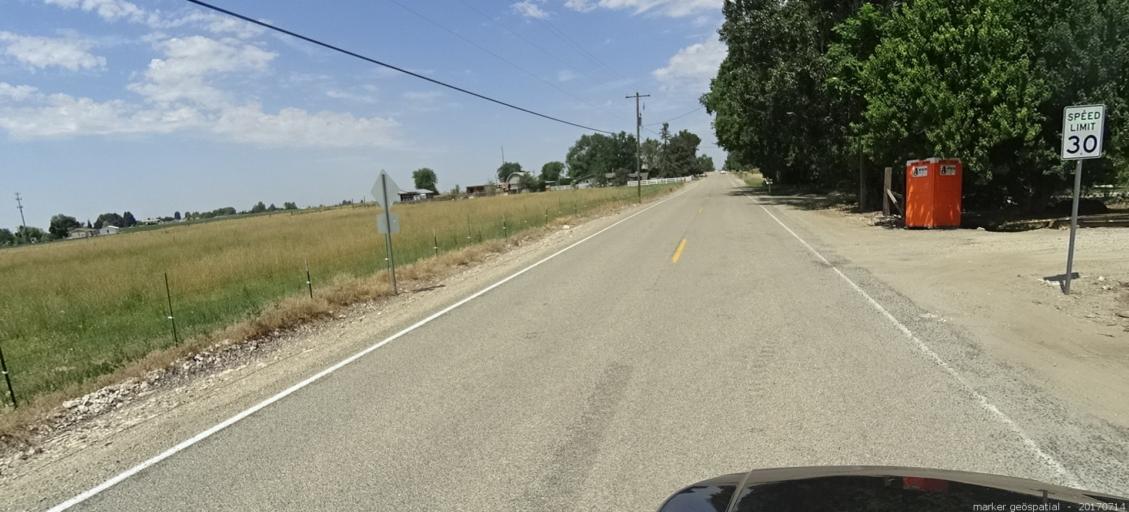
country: US
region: Idaho
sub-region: Ada County
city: Kuna
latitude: 43.5255
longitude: -116.3543
